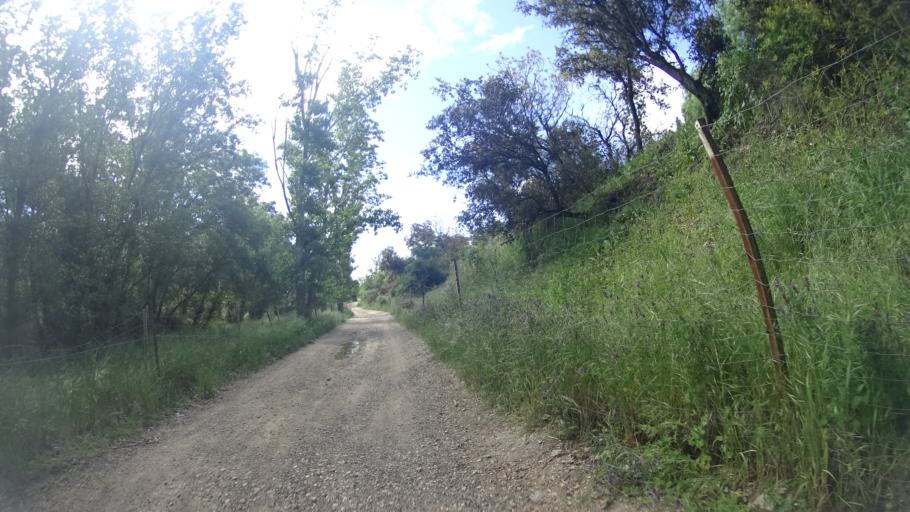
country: ES
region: Madrid
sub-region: Provincia de Madrid
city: Brunete
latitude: 40.4240
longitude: -3.9514
